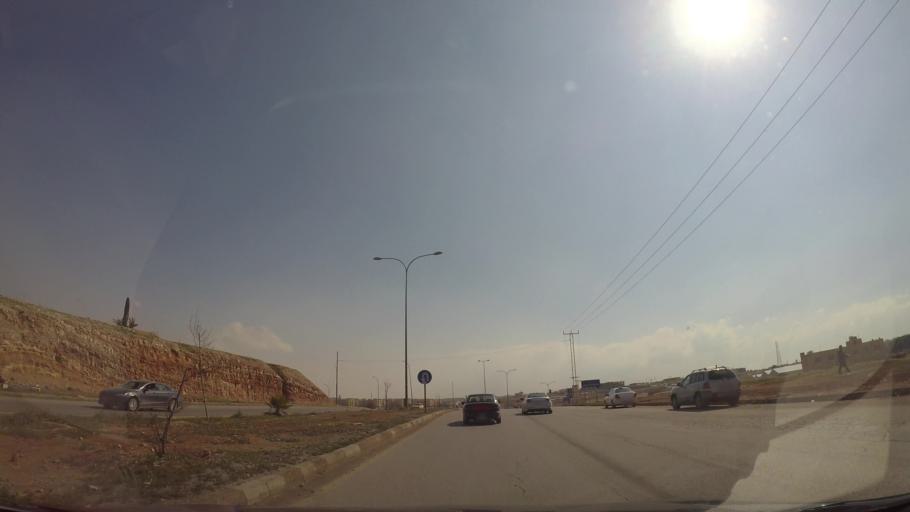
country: JO
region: Zarqa
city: Zarqa
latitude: 32.0742
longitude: 36.1037
